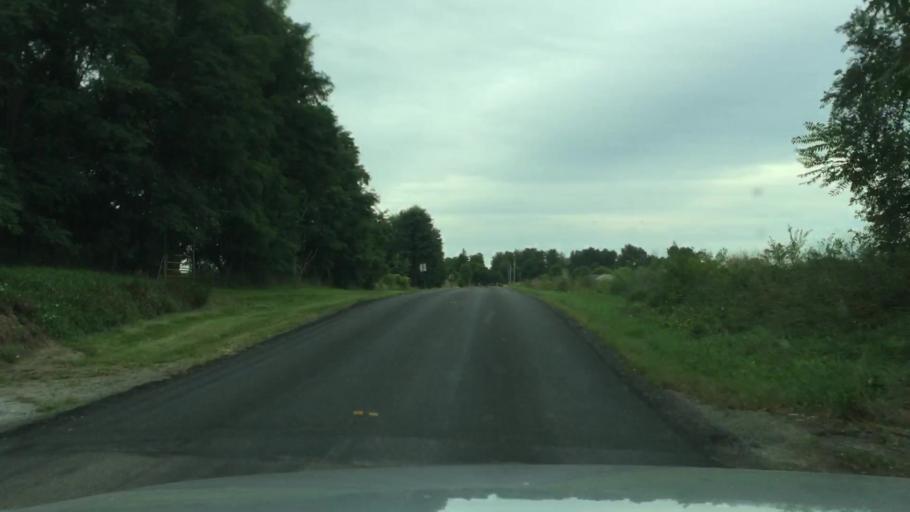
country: US
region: Michigan
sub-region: Shiawassee County
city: Durand
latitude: 42.8773
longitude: -84.0620
